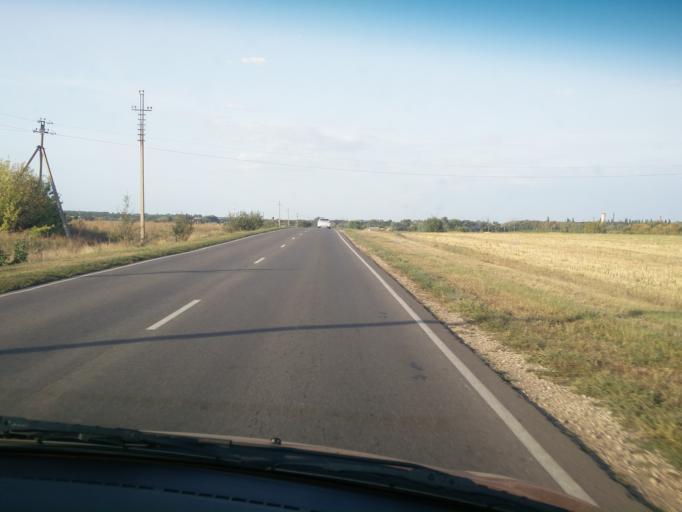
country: RU
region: Voronezj
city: Ramon'
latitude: 51.9322
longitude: 39.3309
